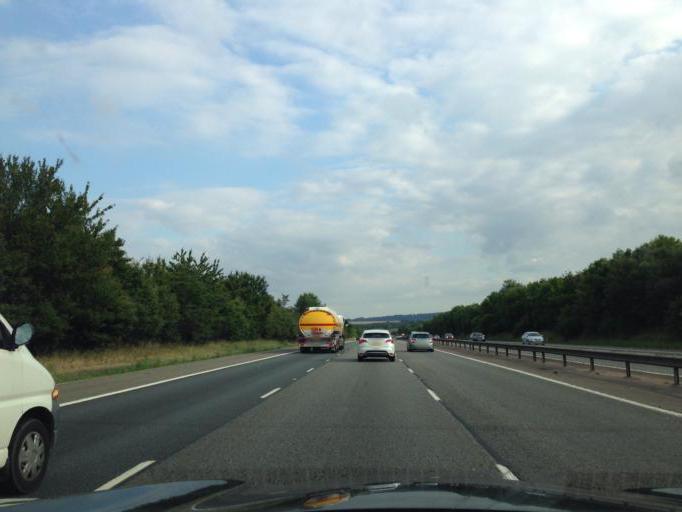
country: GB
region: England
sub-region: Warwickshire
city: Harbury
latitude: 52.1807
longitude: -1.4469
